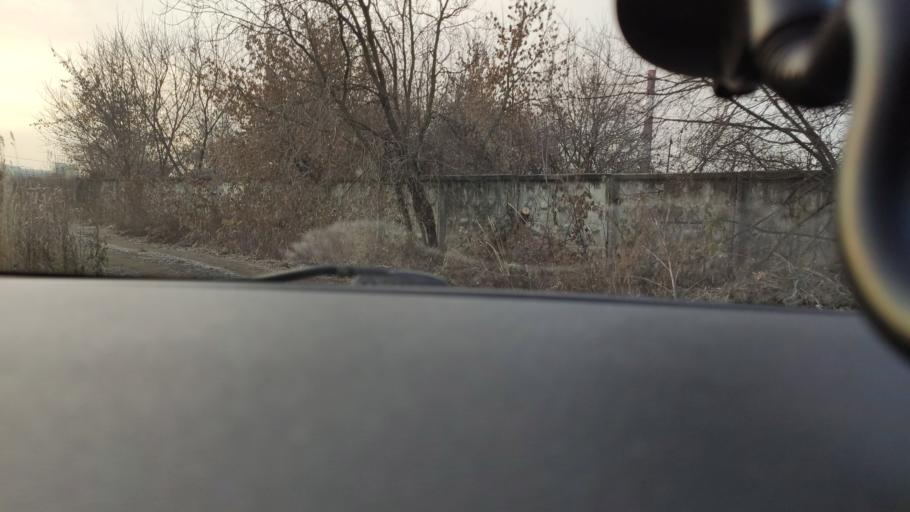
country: RU
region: Perm
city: Kondratovo
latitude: 57.9970
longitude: 56.1138
